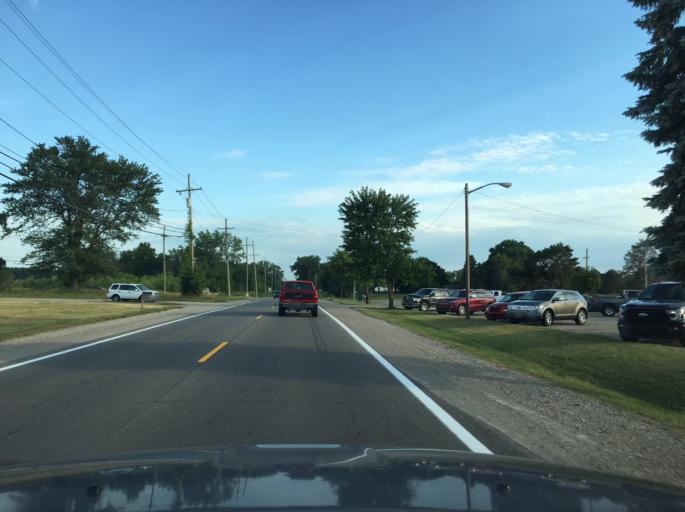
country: US
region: Michigan
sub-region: Macomb County
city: Mount Clemens
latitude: 42.6601
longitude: -82.8774
